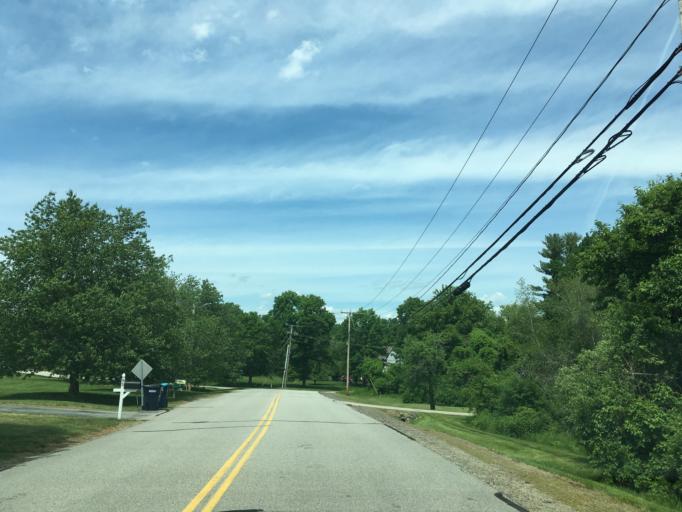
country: US
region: New Hampshire
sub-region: Rockingham County
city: Stratham Station
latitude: 43.0230
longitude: -70.8755
